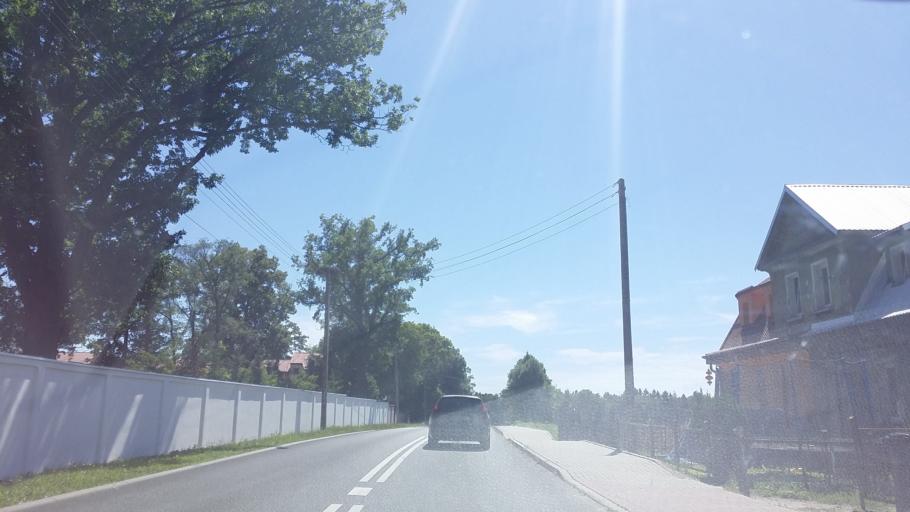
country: PL
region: West Pomeranian Voivodeship
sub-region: Powiat lobeski
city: Wegorzyno
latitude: 53.5127
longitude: 15.5740
